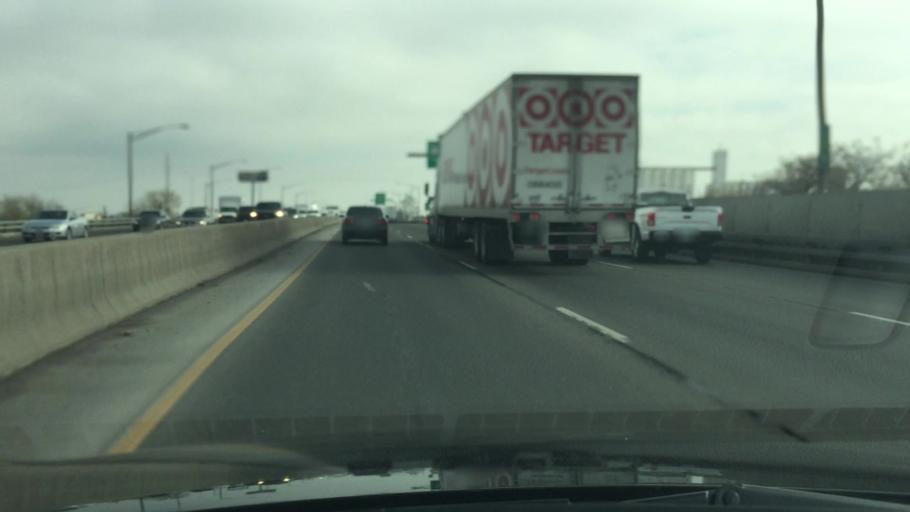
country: US
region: Colorado
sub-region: Adams County
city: Commerce City
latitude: 39.7800
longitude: -104.9543
